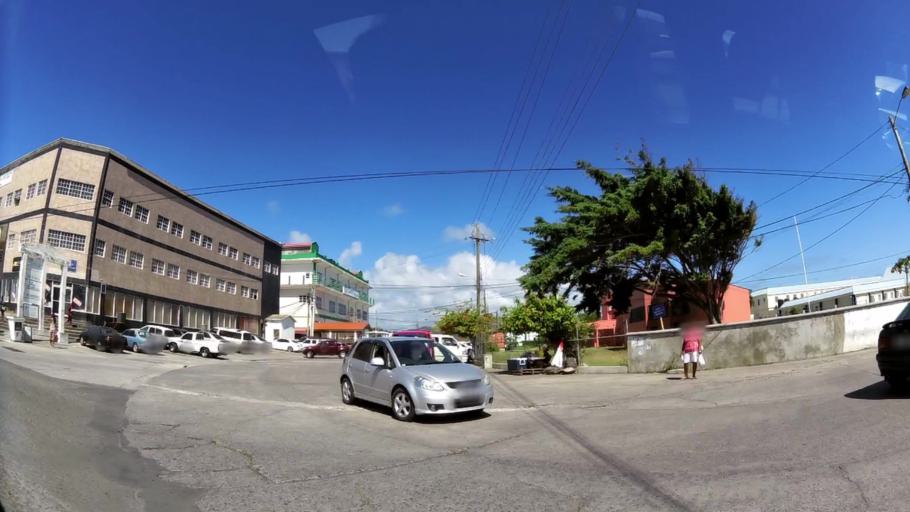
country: LC
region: Vieux-Fort
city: Vieux Fort
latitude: 13.7298
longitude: -60.9503
